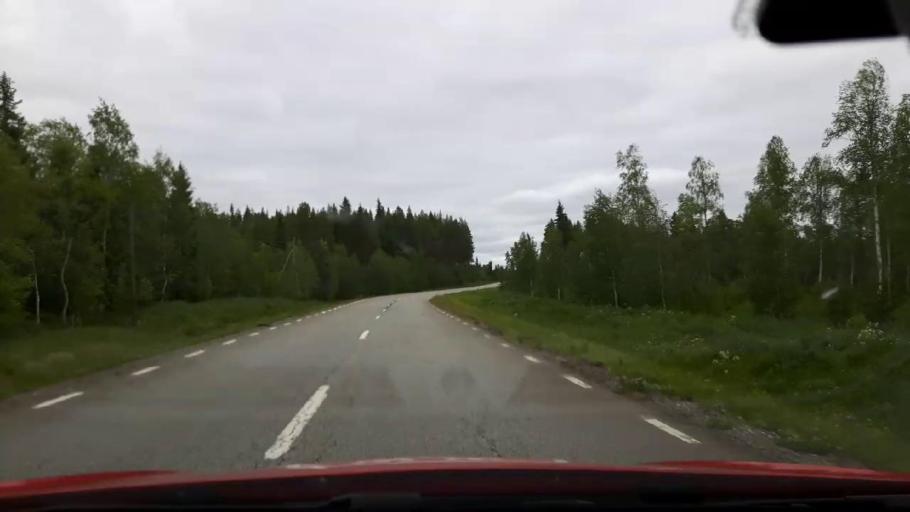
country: SE
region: Jaemtland
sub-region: Stroemsunds Kommun
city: Stroemsund
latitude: 63.3826
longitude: 15.6841
